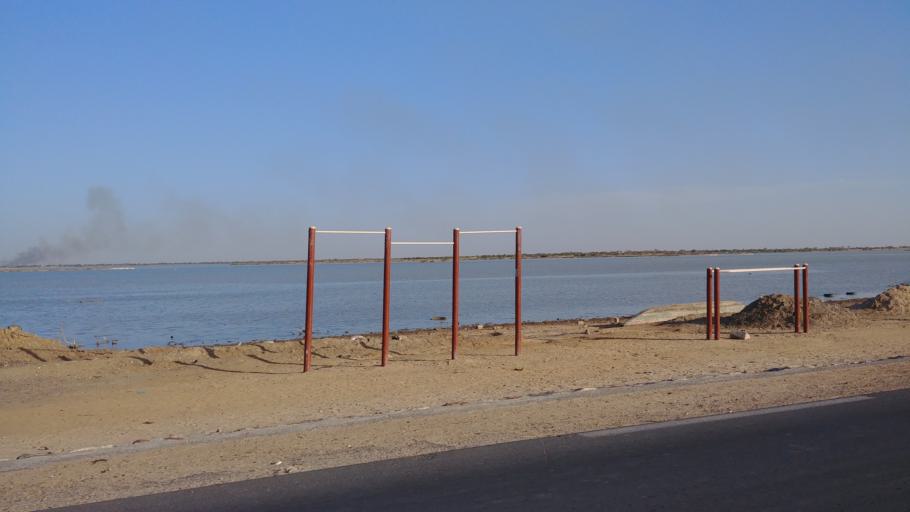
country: SN
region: Saint-Louis
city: Saint-Louis
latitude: 16.0214
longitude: -16.4829
